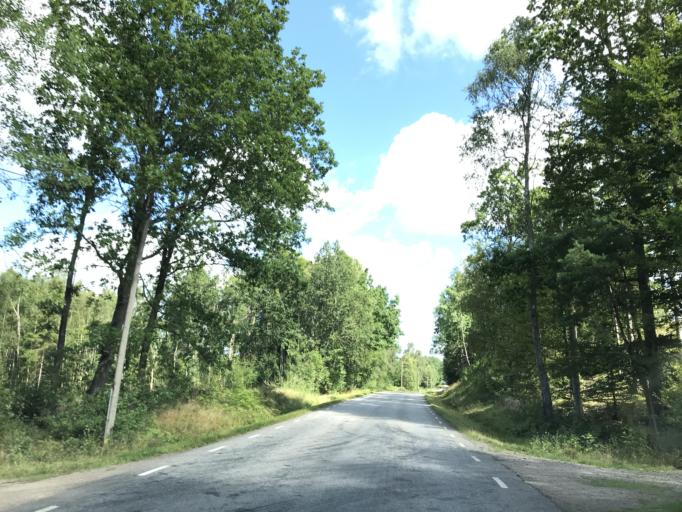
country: SE
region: Halland
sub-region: Laholms Kommun
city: Knared
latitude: 56.4413
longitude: 13.3122
